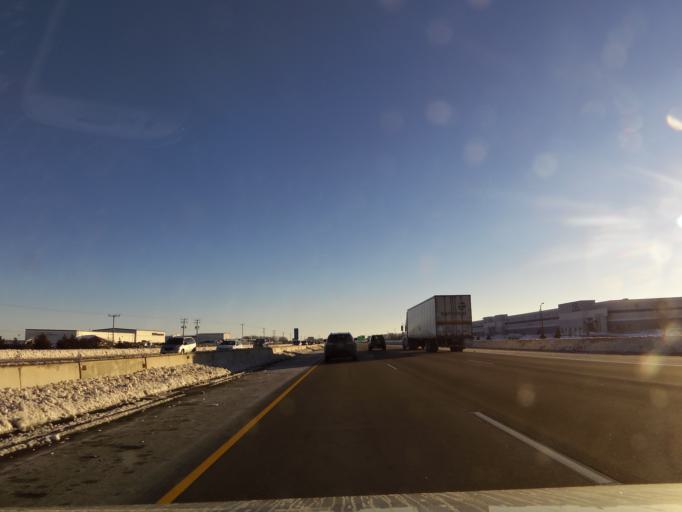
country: US
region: Wisconsin
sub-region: Racine County
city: Franksville
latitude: 42.7158
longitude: -87.9540
